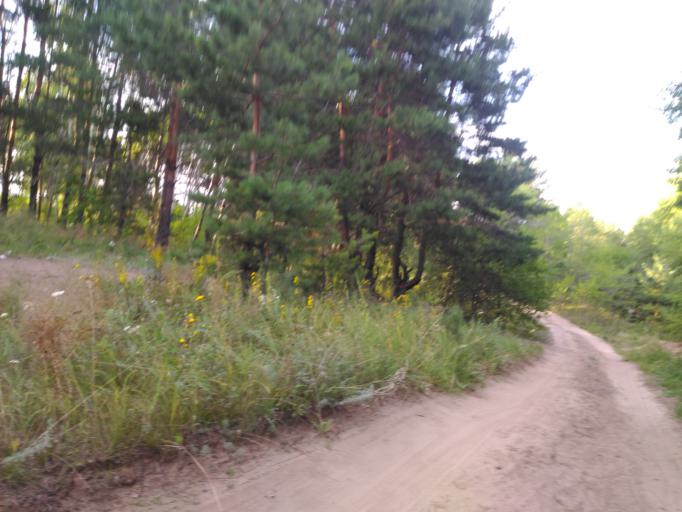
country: RU
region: Ulyanovsk
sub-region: Ulyanovskiy Rayon
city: Ulyanovsk
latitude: 54.3537
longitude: 48.5155
